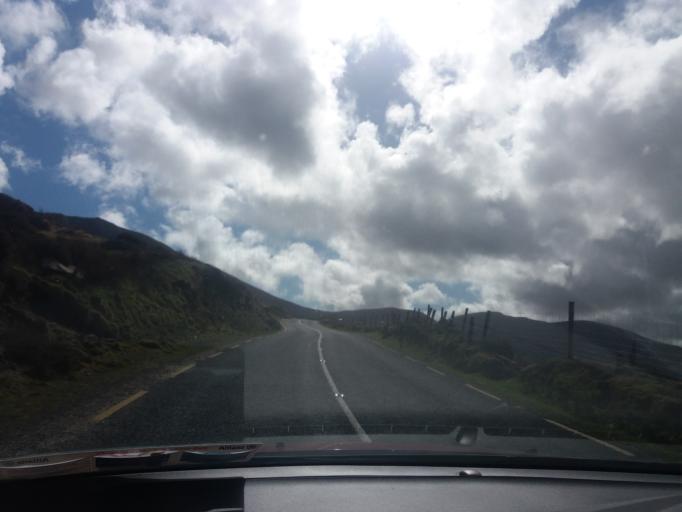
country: IE
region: Munster
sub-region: Ciarrai
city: Dingle
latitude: 52.1999
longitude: -10.1791
